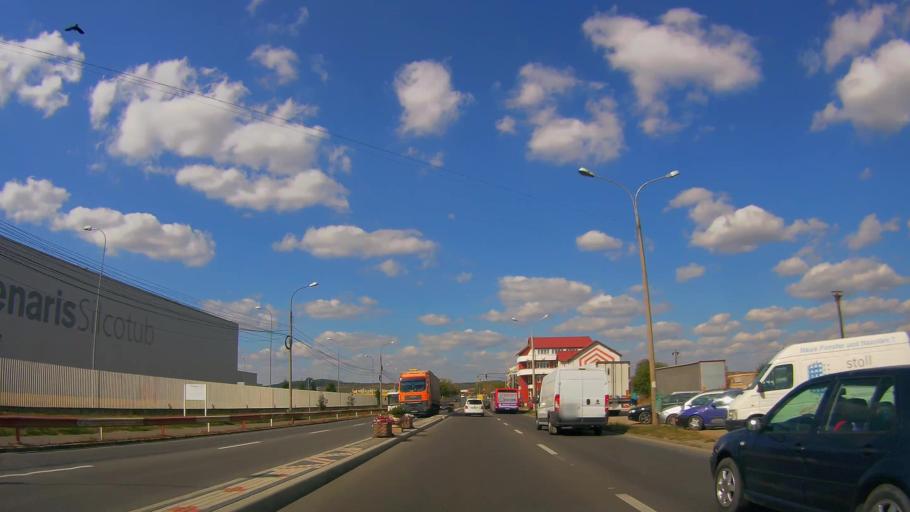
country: RO
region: Salaj
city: Zalau
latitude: 47.2132
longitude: 23.0431
